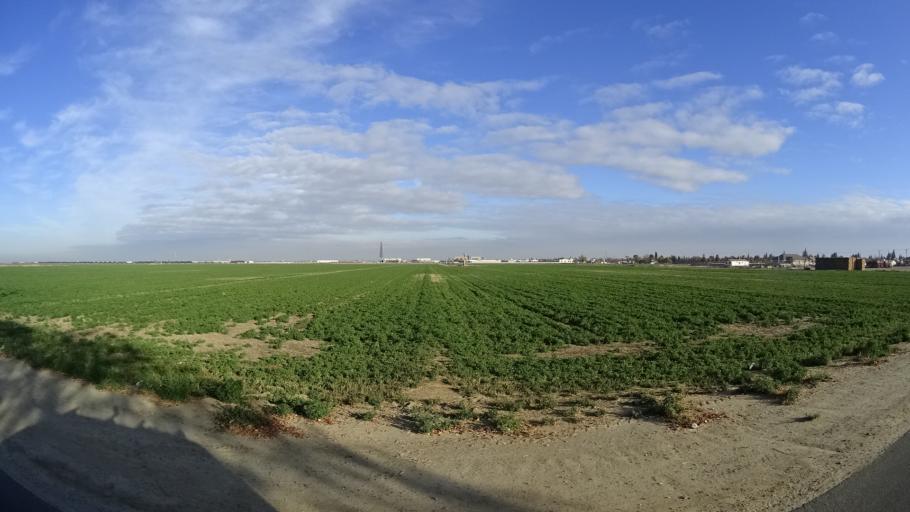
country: US
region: California
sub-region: Kern County
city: Rosedale
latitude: 35.3035
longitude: -119.1315
